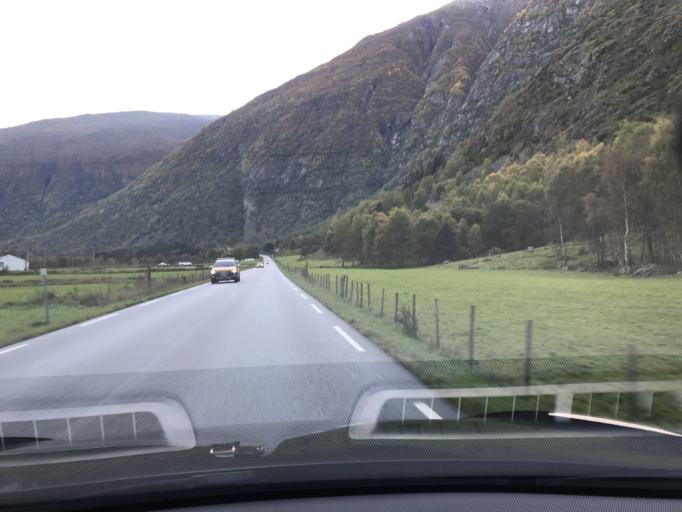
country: NO
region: Sogn og Fjordane
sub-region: Laerdal
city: Laerdalsoyri
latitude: 61.0818
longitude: 7.5071
